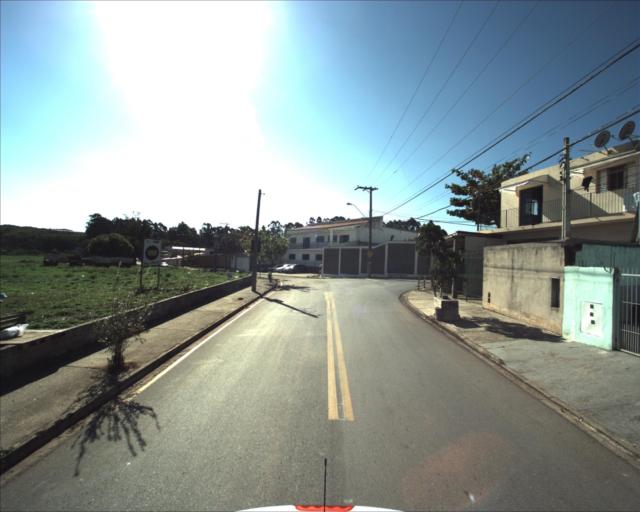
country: BR
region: Sao Paulo
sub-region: Sorocaba
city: Sorocaba
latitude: -23.4632
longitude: -47.4435
